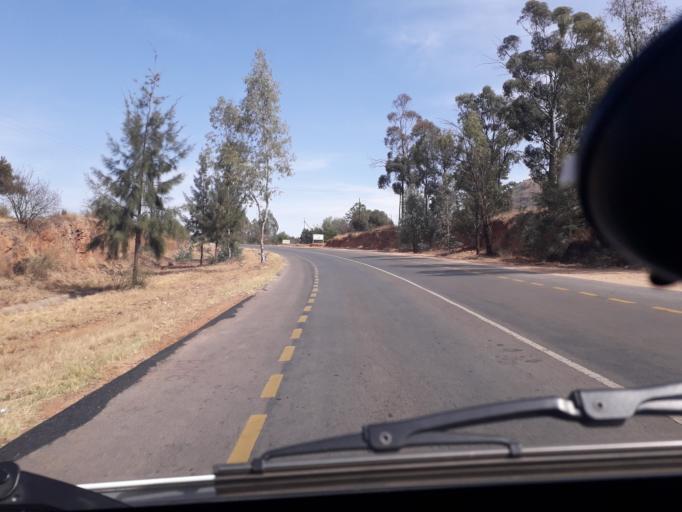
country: ZA
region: Gauteng
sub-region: West Rand District Municipality
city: Muldersdriseloop
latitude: -25.9886
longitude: 27.8410
